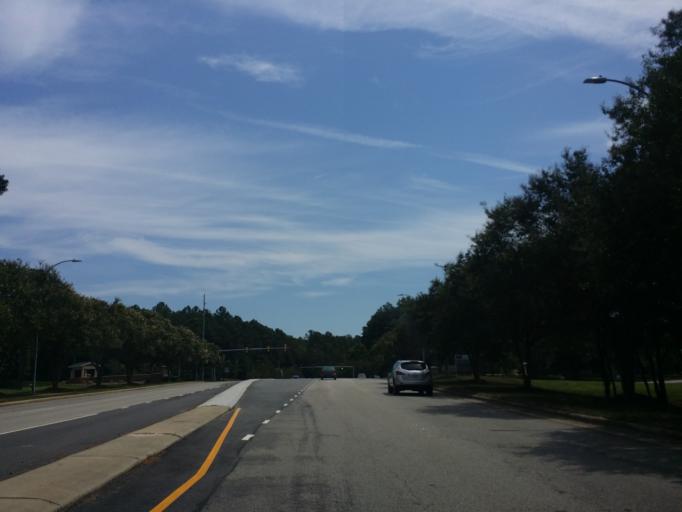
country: US
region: North Carolina
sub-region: Wake County
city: Morrisville
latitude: 35.8275
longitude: -78.8072
